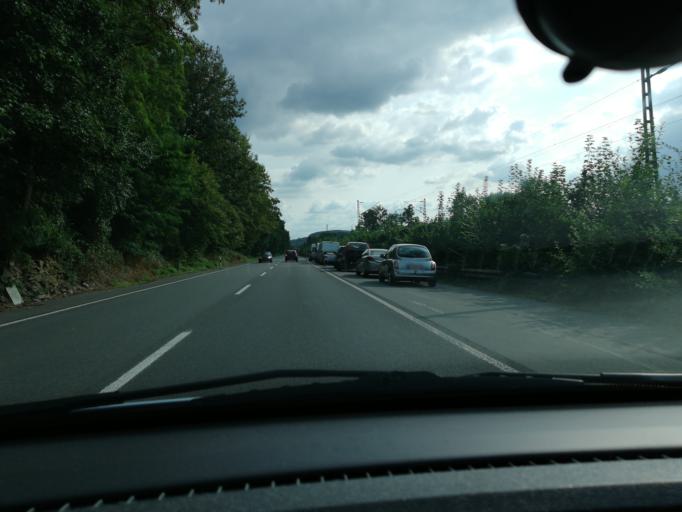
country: DE
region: North Rhine-Westphalia
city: Witten
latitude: 51.4205
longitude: 7.3538
